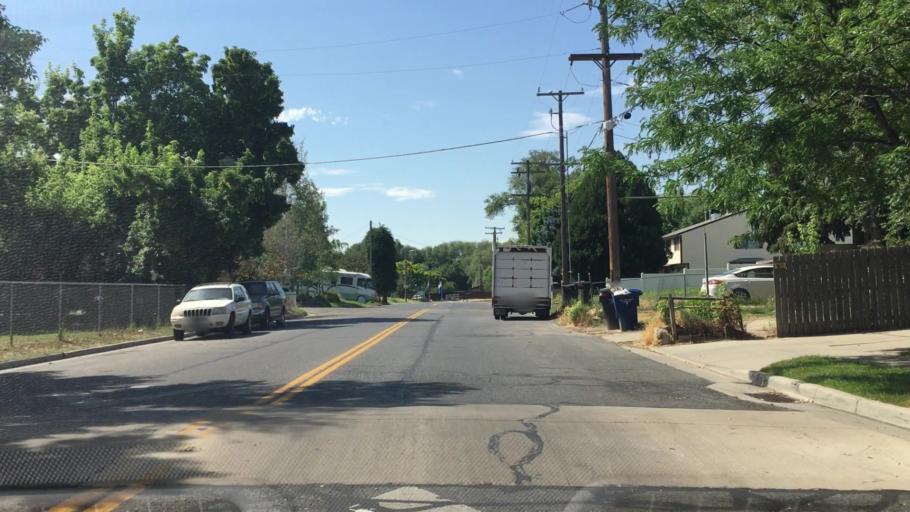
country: US
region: Utah
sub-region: Salt Lake County
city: Millcreek
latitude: 40.6834
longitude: -111.8828
